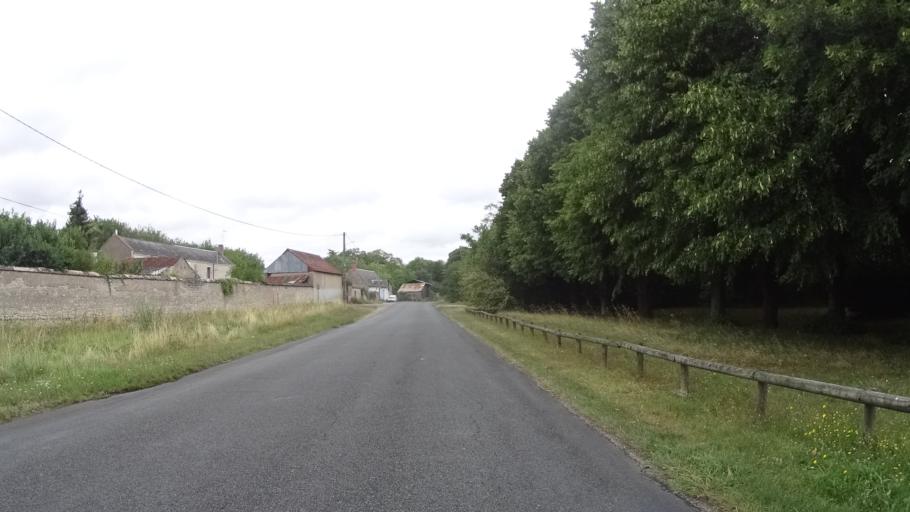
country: FR
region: Centre
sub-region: Departement du Loiret
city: Meung-sur-Loire
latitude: 47.8170
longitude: 1.6898
